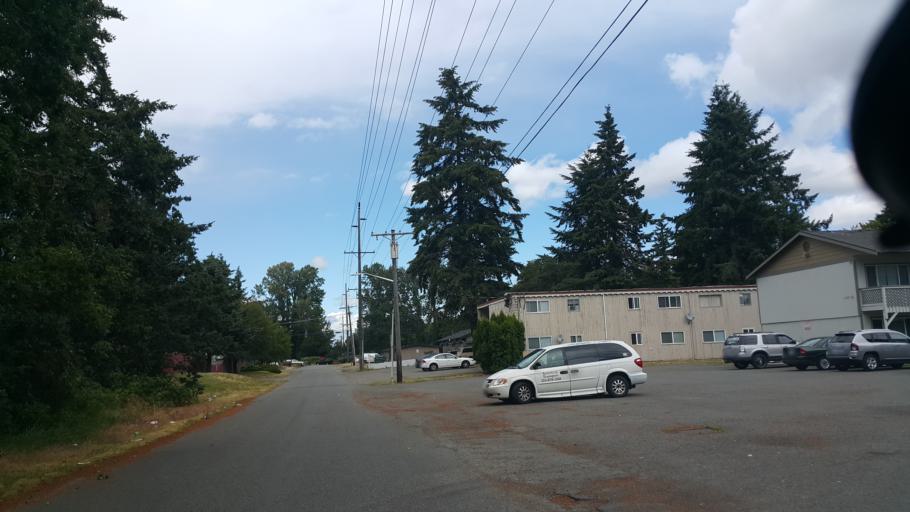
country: US
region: Washington
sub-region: Pierce County
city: McChord Air Force Base
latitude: 47.1410
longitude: -122.4993
